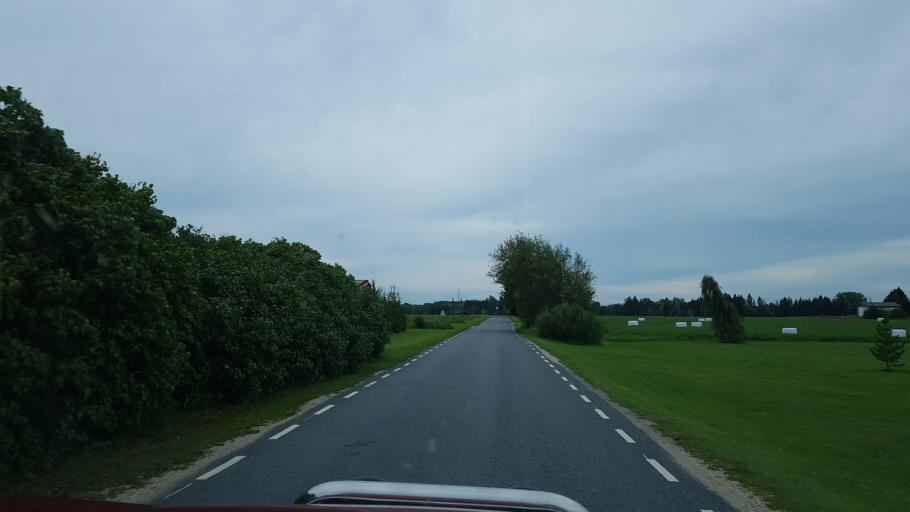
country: EE
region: Harju
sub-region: Nissi vald
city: Turba
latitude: 58.8778
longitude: 24.0799
